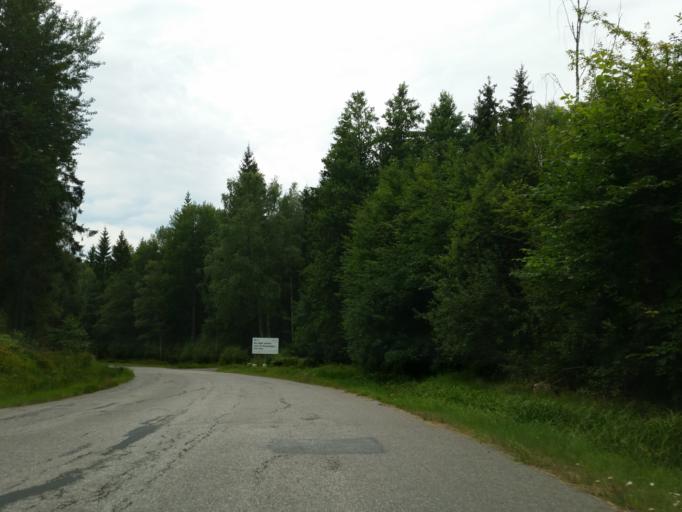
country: SE
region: Stockholm
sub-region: Sodertalje Kommun
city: Soedertaelje
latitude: 59.2154
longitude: 17.6565
